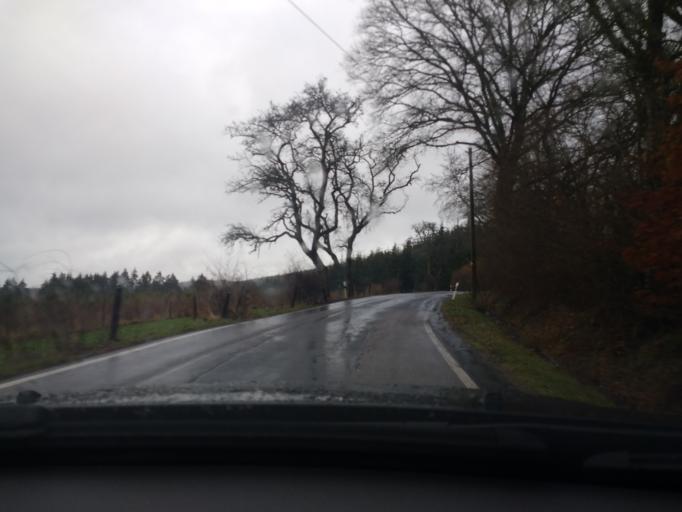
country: DE
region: Rheinland-Pfalz
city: Heddert
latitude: 49.6433
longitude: 6.7315
